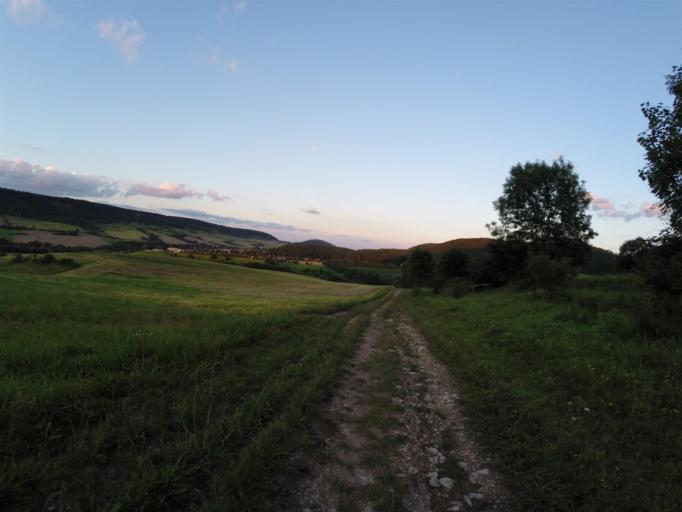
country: DE
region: Thuringia
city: Grosslobichau
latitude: 50.9246
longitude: 11.6394
